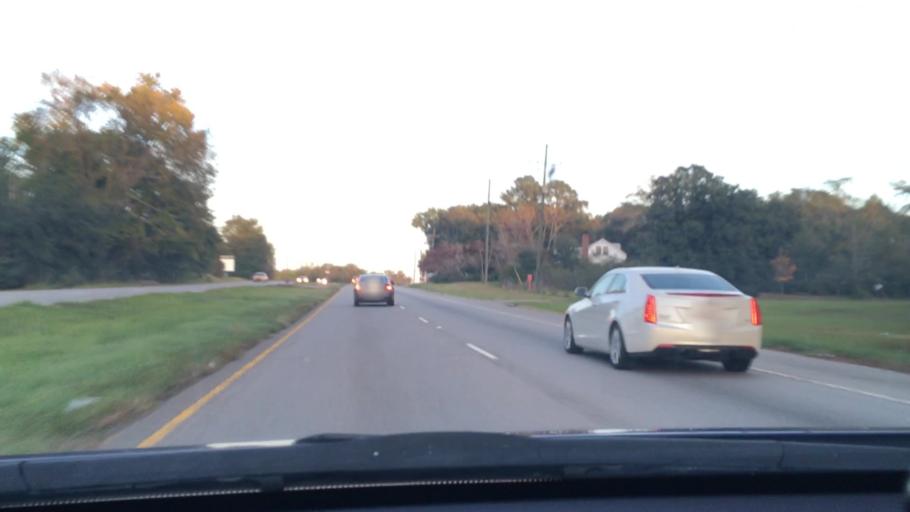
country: US
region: South Carolina
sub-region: Richland County
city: Hopkins
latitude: 33.9442
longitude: -80.8948
